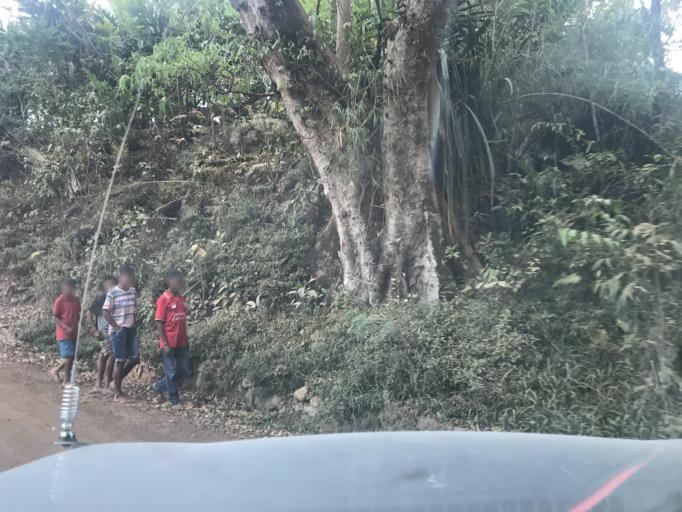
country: TL
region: Ainaro
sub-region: Ainaro
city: Ainaro
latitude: -8.9981
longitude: 125.5030
